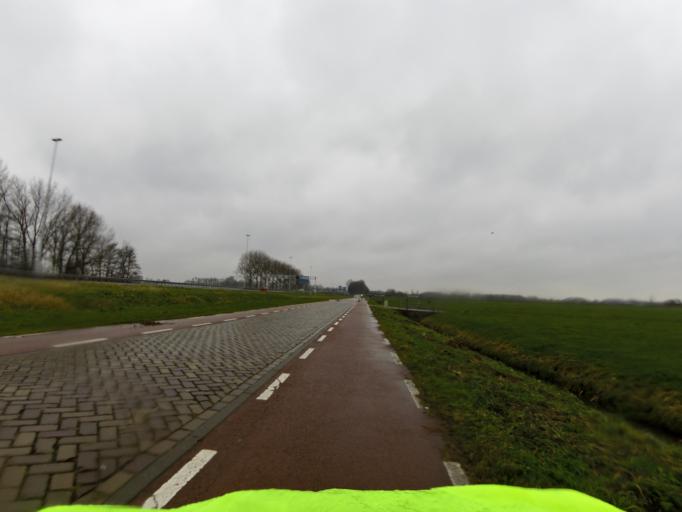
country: NL
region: South Holland
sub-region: Gemeente Maassluis
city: Maassluis
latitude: 51.9225
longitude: 4.2854
